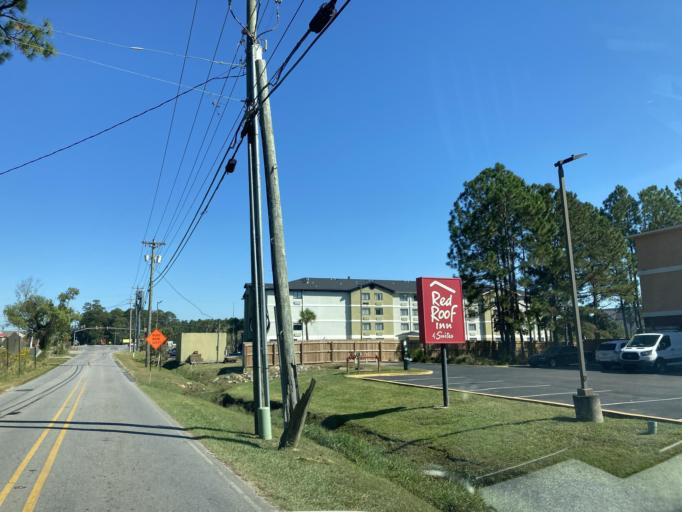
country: US
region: Mississippi
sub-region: Jackson County
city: Gulf Hills
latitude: 30.4576
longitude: -88.8459
